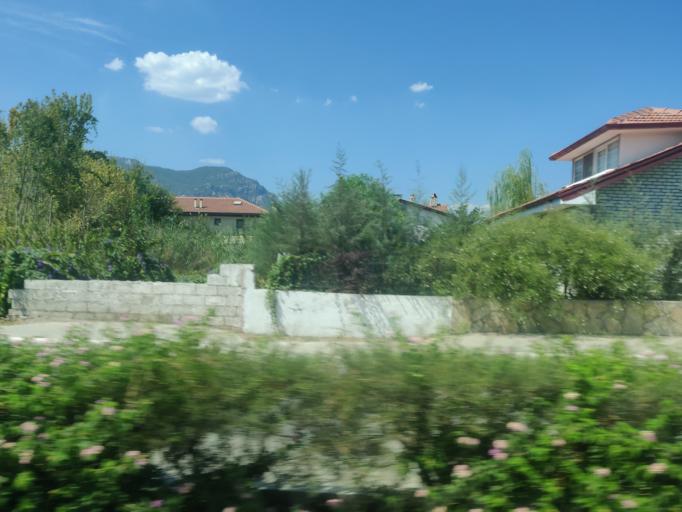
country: TR
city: Dalyan
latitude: 36.8393
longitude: 28.6501
